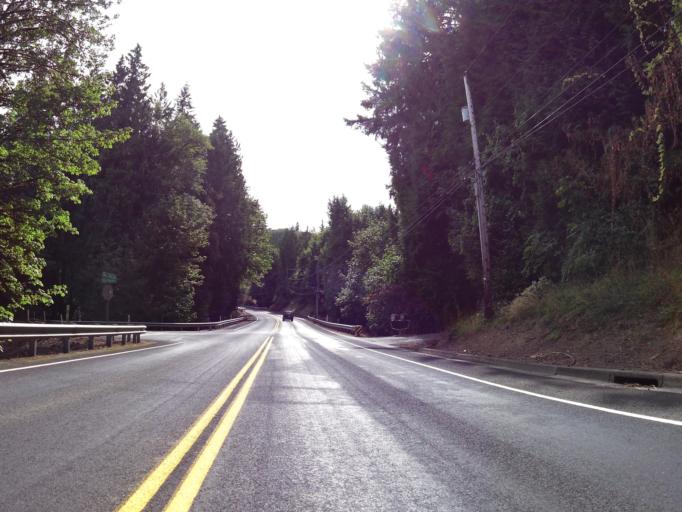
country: US
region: Washington
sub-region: Cowlitz County
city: Castle Rock
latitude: 46.3236
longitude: -122.9296
